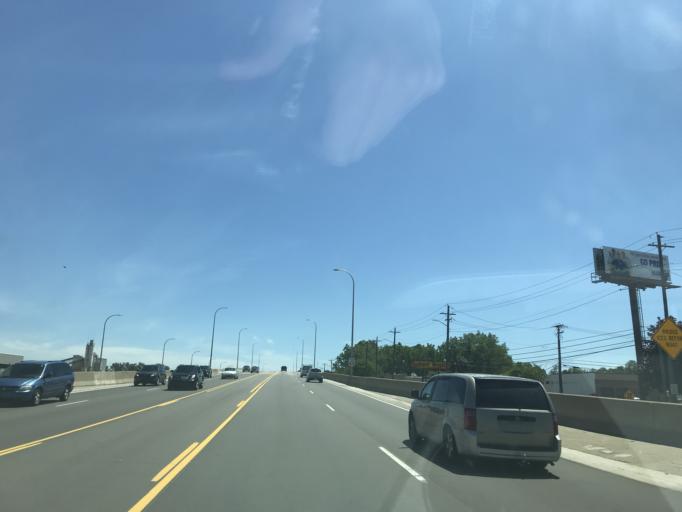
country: US
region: Michigan
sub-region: Wayne County
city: Westland
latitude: 42.3233
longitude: -83.4281
